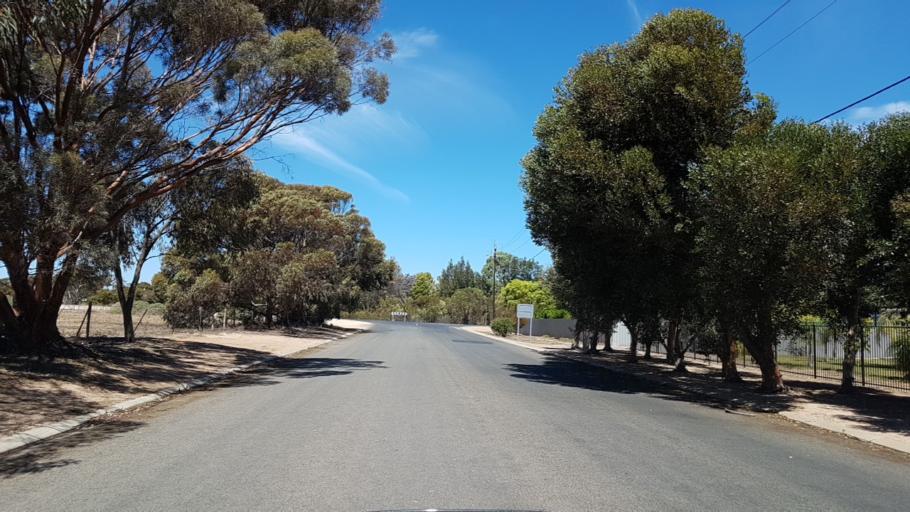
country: AU
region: South Australia
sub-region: Copper Coast
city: Wallaroo
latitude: -34.0589
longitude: 137.5841
